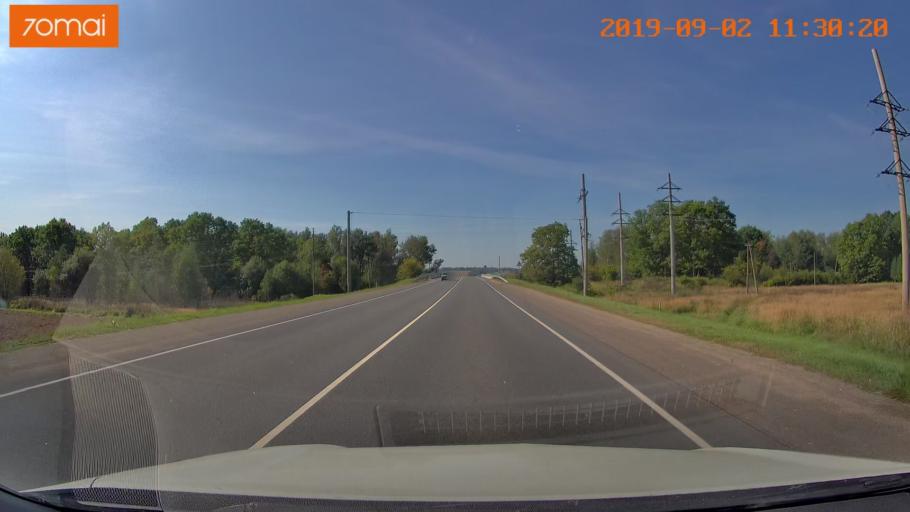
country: RU
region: Smolensk
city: Roslavl'
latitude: 53.9853
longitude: 32.8366
